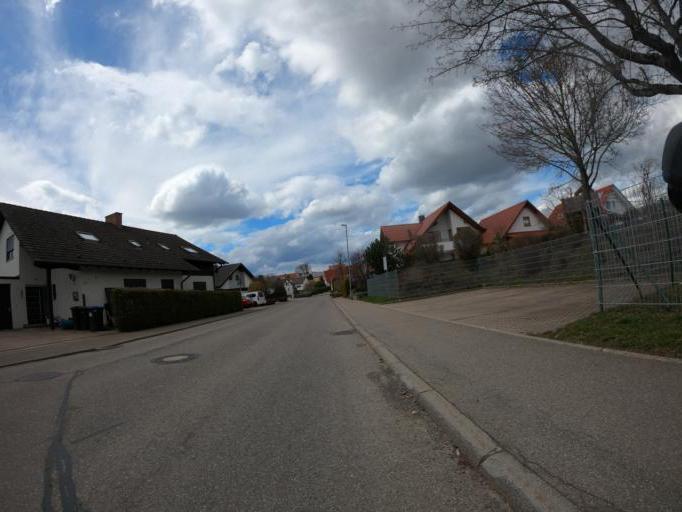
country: DE
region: Baden-Wuerttemberg
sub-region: Tuebingen Region
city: Pfullingen
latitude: 48.3904
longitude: 9.1850
